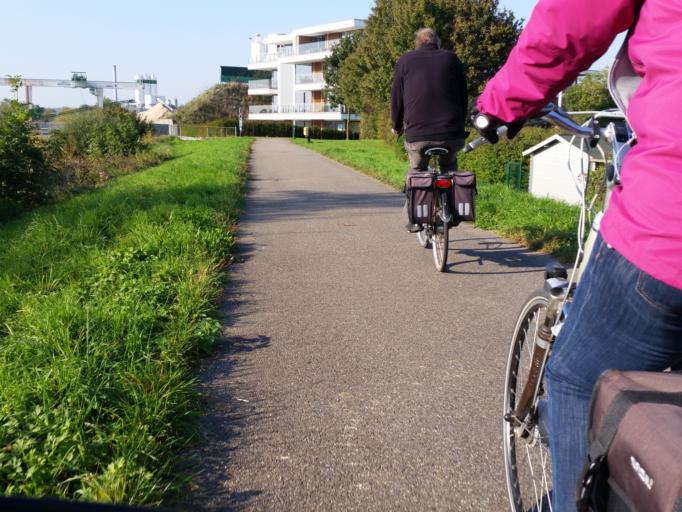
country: BE
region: Flanders
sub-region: Provincie Antwerpen
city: Rumst
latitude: 51.0768
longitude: 4.4187
